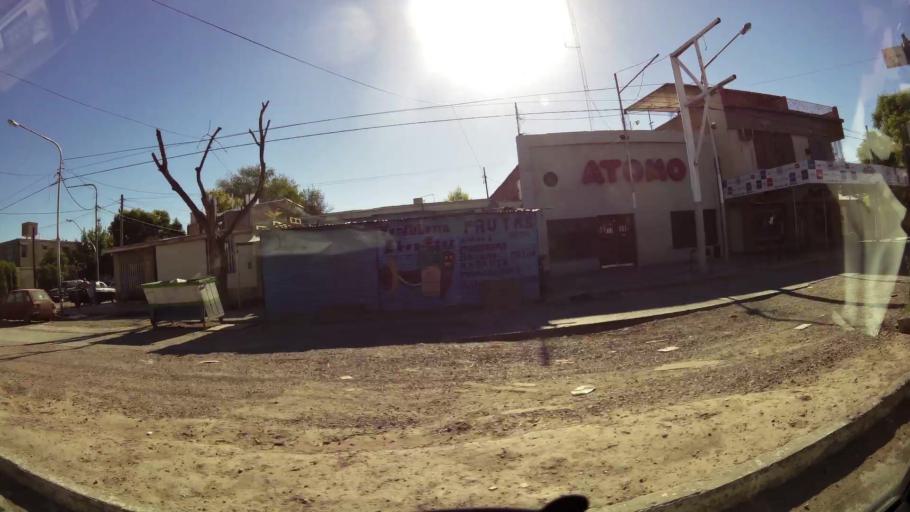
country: AR
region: Mendoza
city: Las Heras
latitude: -32.8610
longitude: -68.8216
